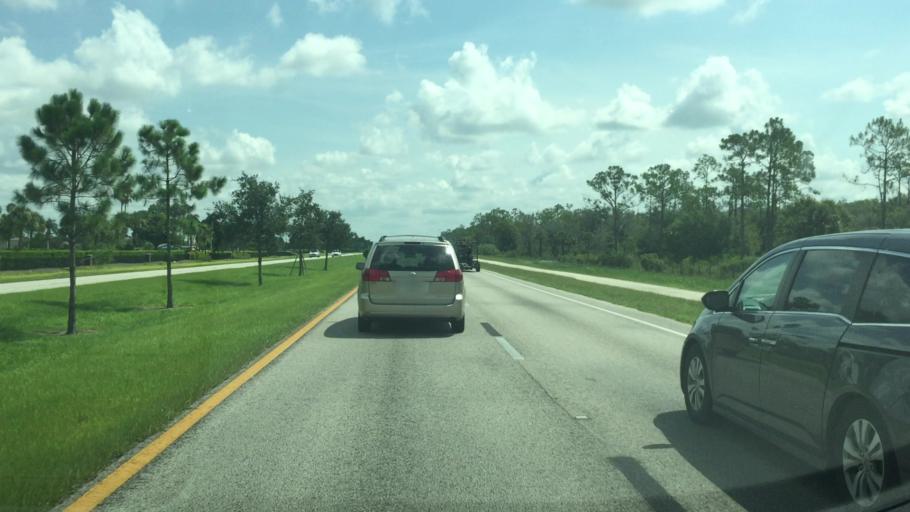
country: US
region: Florida
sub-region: Lee County
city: Fort Myers
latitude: 26.5843
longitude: -81.8206
